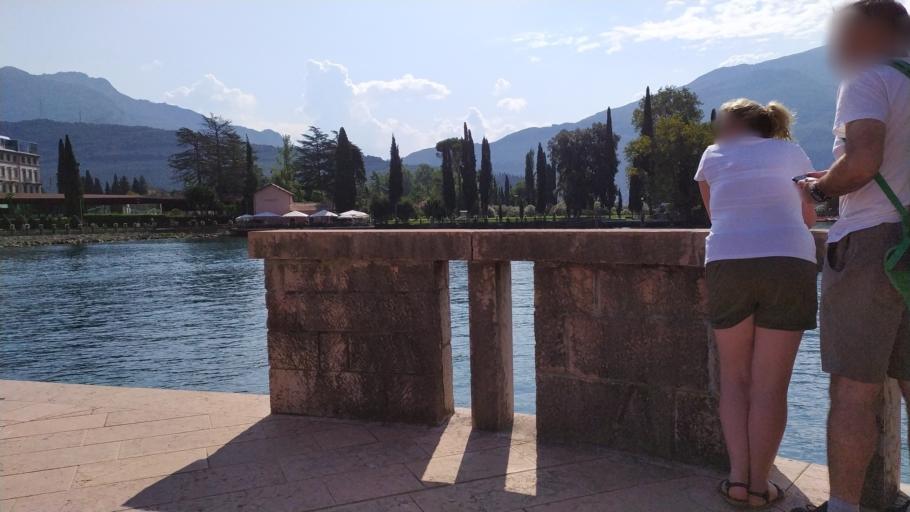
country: IT
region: Trentino-Alto Adige
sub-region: Provincia di Trento
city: Riva del Garda
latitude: 45.8828
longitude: 10.8439
